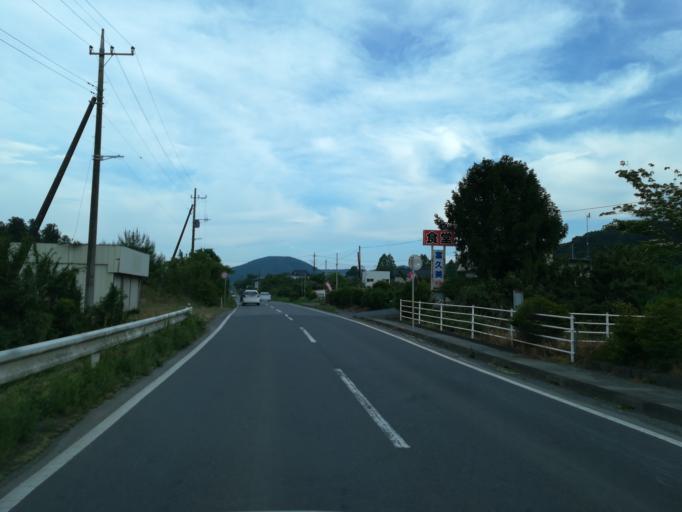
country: JP
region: Ibaraki
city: Tsukuba
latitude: 36.2171
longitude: 140.1694
